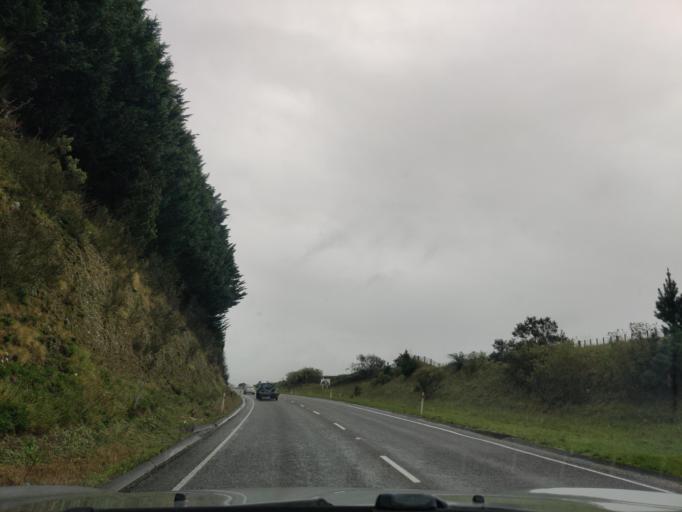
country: NZ
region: Manawatu-Wanganui
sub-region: Palmerston North City
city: Palmerston North
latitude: -40.0545
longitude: 176.2348
